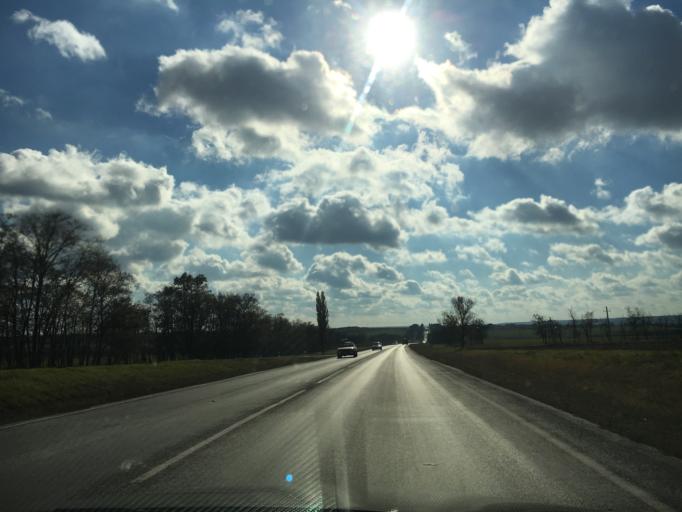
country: RU
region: Rostov
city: Matveyev Kurgan
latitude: 47.5587
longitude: 38.8894
